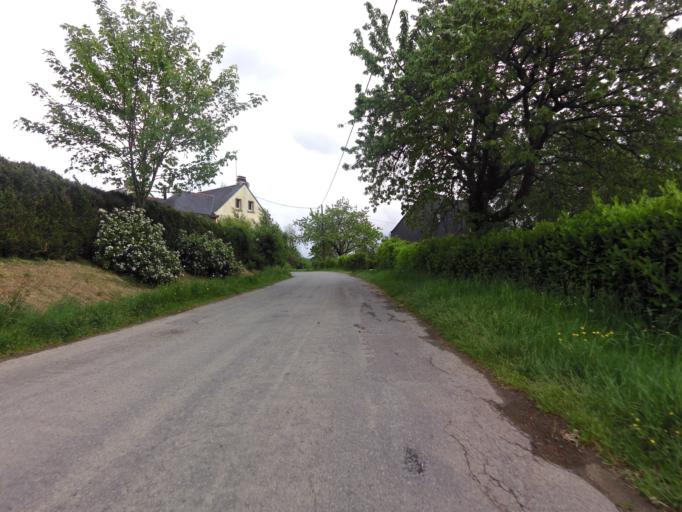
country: FR
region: Brittany
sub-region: Departement du Morbihan
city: Molac
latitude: 47.7319
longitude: -2.4568
